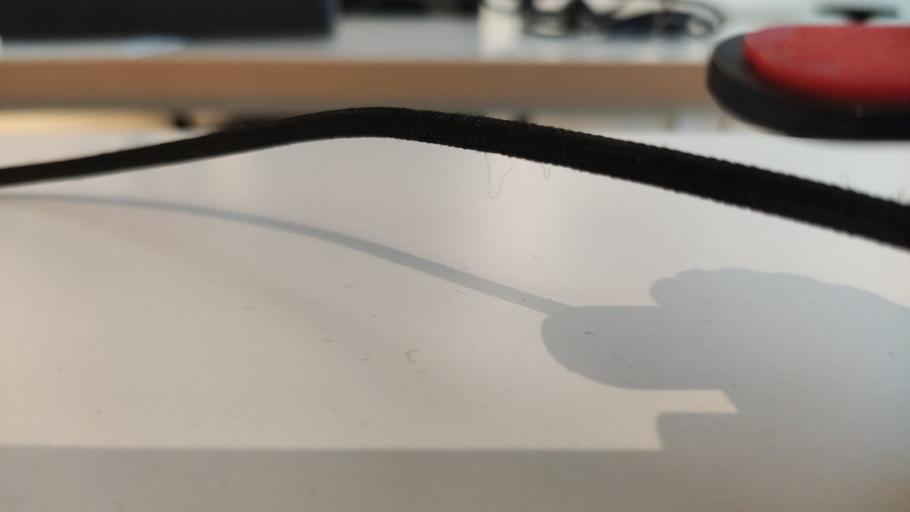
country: RU
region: Moskovskaya
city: Novopetrovskoye
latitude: 55.9128
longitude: 36.4412
